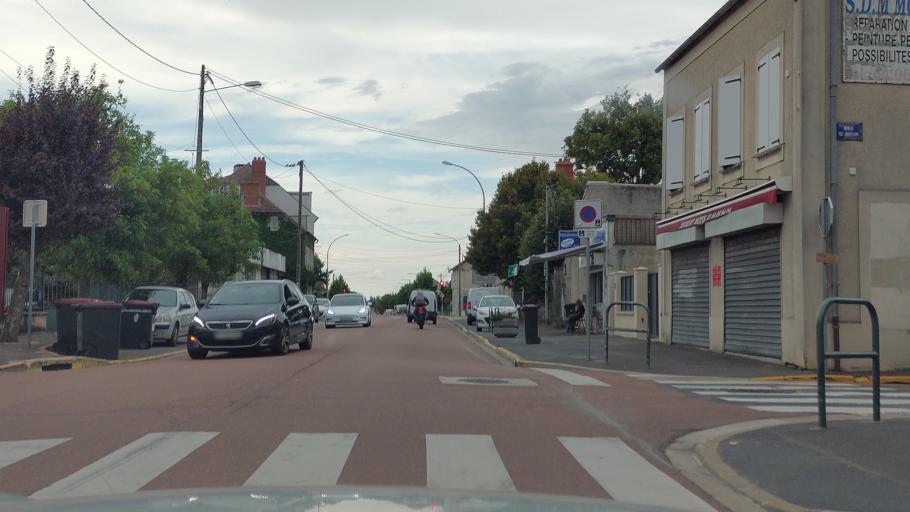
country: FR
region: Ile-de-France
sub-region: Departement de Seine-et-Marne
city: Mormant
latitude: 48.6095
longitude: 2.8907
